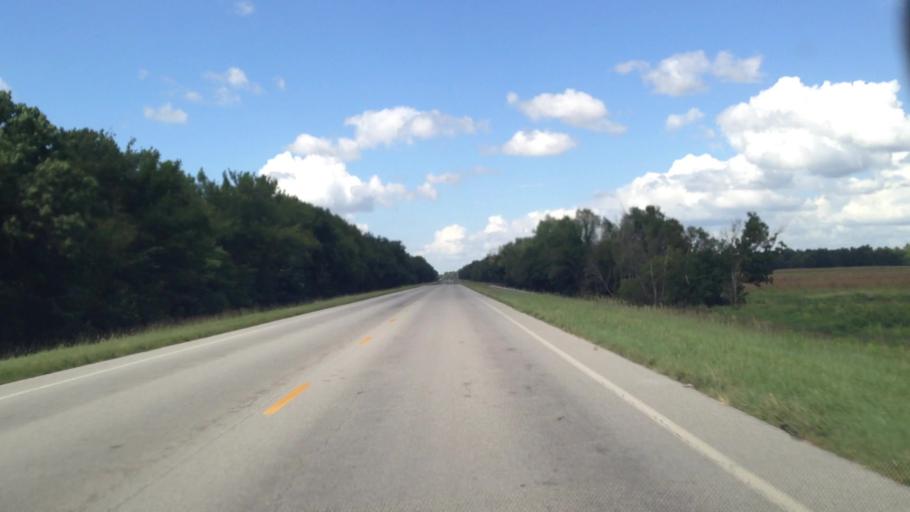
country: US
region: Kansas
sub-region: Labette County
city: Chetopa
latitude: 37.0656
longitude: -95.1031
